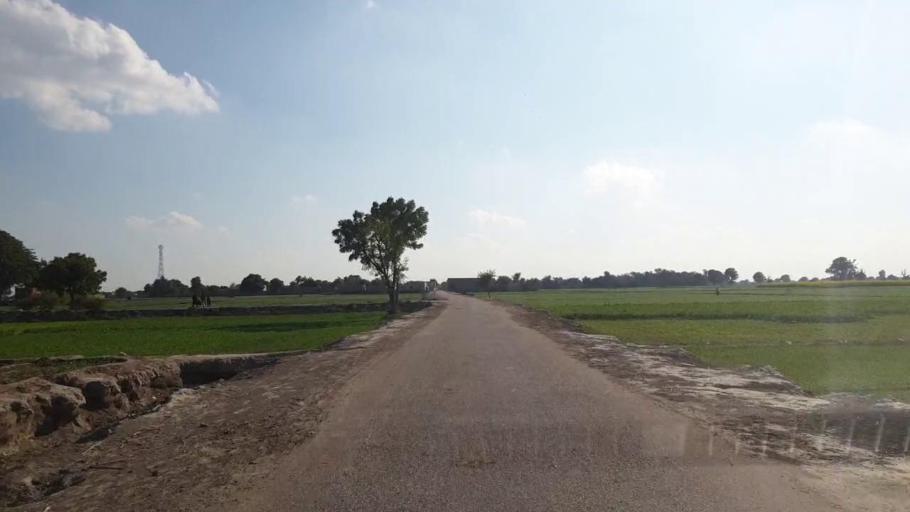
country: PK
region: Sindh
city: Shahpur Chakar
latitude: 26.1083
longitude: 68.5645
